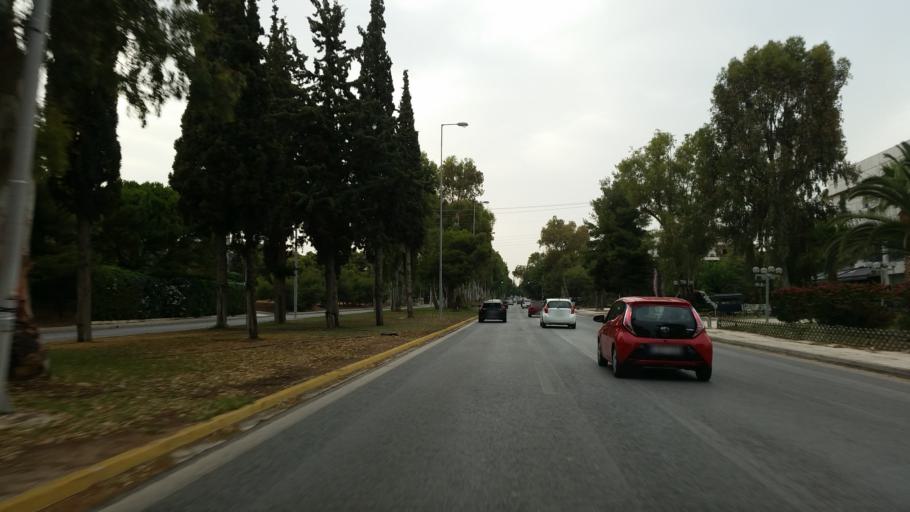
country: GR
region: Attica
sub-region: Nomarchia Anatolikis Attikis
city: Vouliagmeni
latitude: 37.8164
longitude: 23.7782
